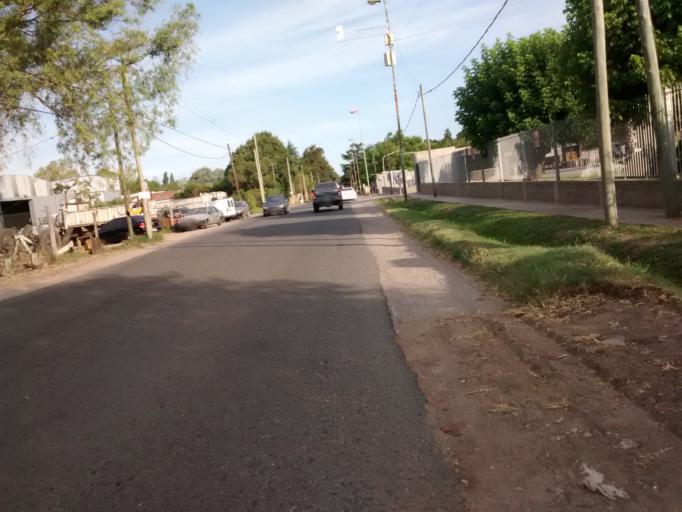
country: AR
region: Buenos Aires
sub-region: Partido de La Plata
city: La Plata
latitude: -34.8668
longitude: -58.1037
